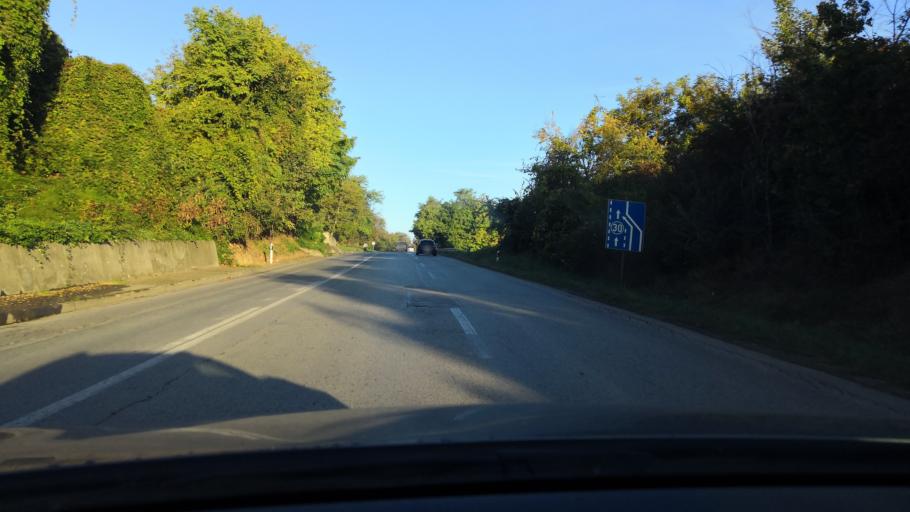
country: RS
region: Autonomna Pokrajina Vojvodina
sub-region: Juznobacki Okrug
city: Sremski Karlovci
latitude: 45.2191
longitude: 19.9055
